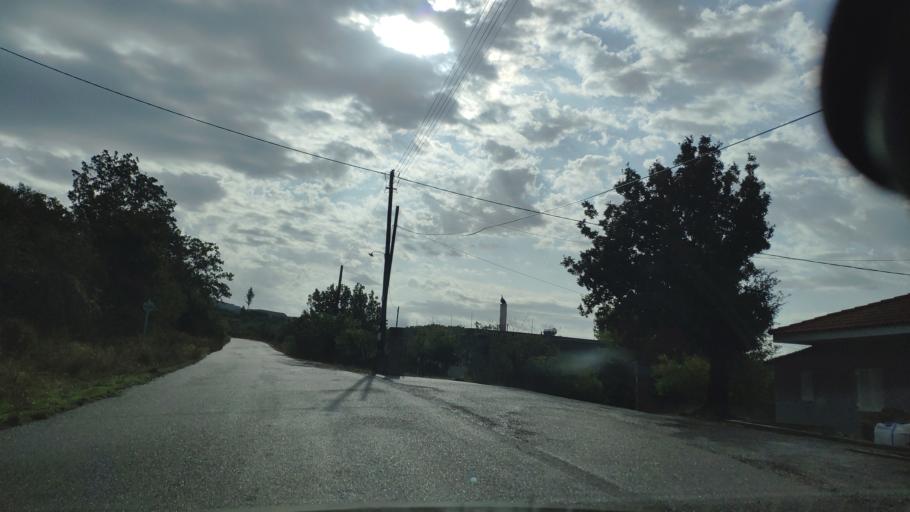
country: GR
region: West Greece
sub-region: Nomos Aitolias kai Akarnanias
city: Sardinia
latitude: 38.8870
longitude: 21.2116
